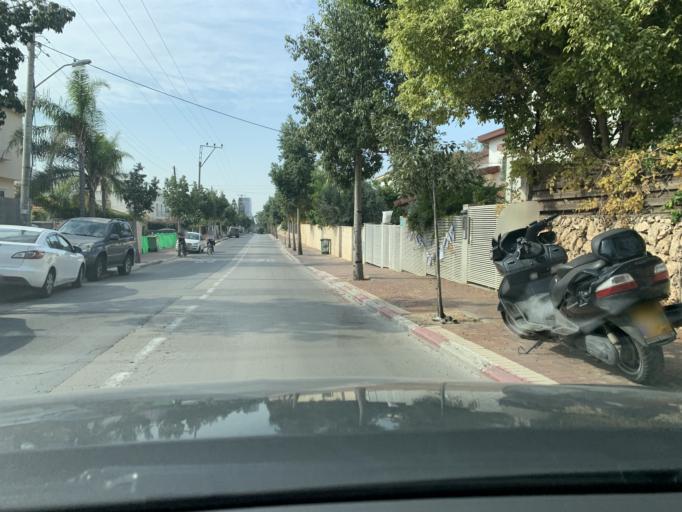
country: IL
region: Central District
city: Ganne Tiqwa
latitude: 32.0603
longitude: 34.8597
